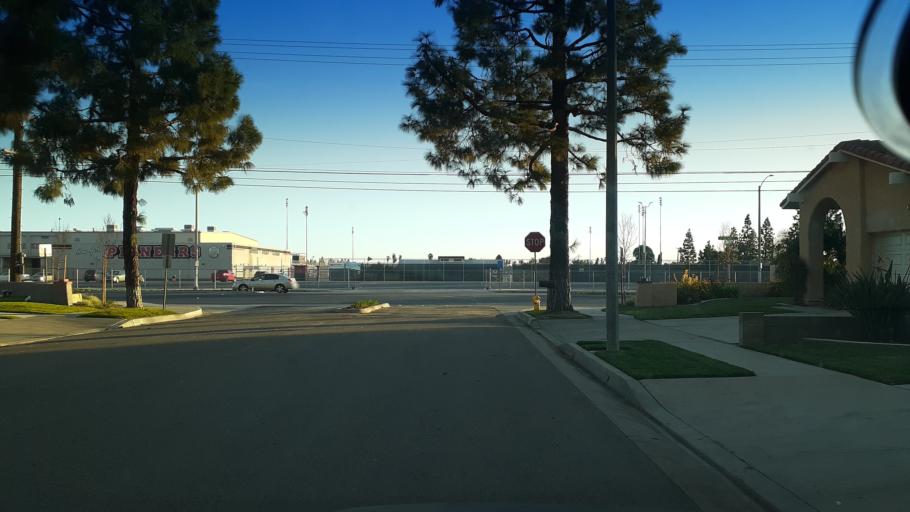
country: US
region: California
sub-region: Los Angeles County
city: Hawaiian Gardens
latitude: 33.8465
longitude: -118.0763
